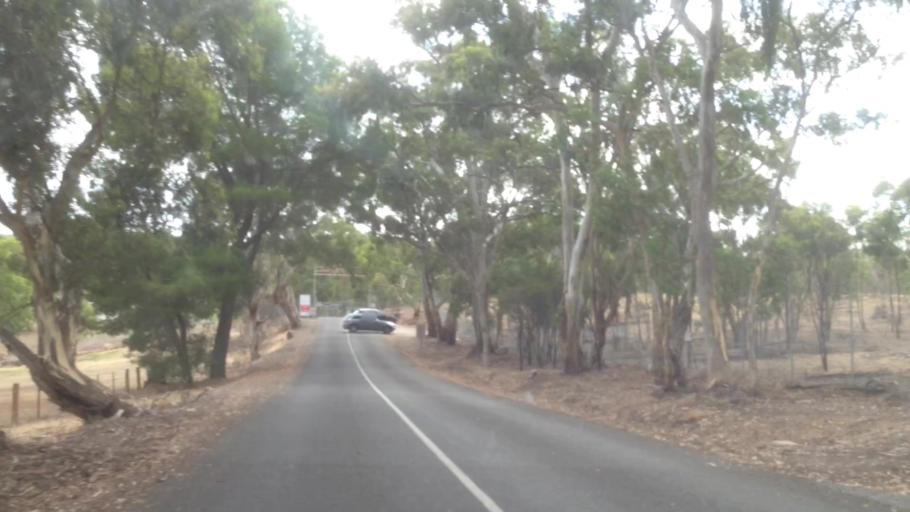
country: AU
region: South Australia
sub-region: Barossa
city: Williamstown
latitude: -34.6435
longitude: 138.8508
